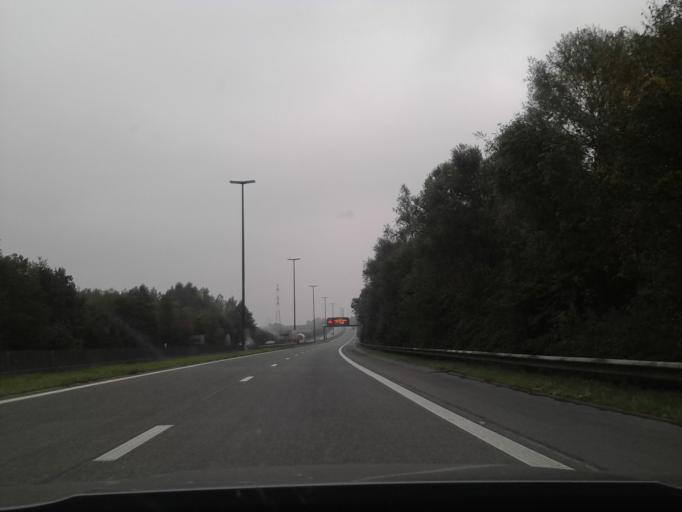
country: BE
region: Wallonia
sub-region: Province du Hainaut
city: Lessines
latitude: 50.6787
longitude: 3.8250
